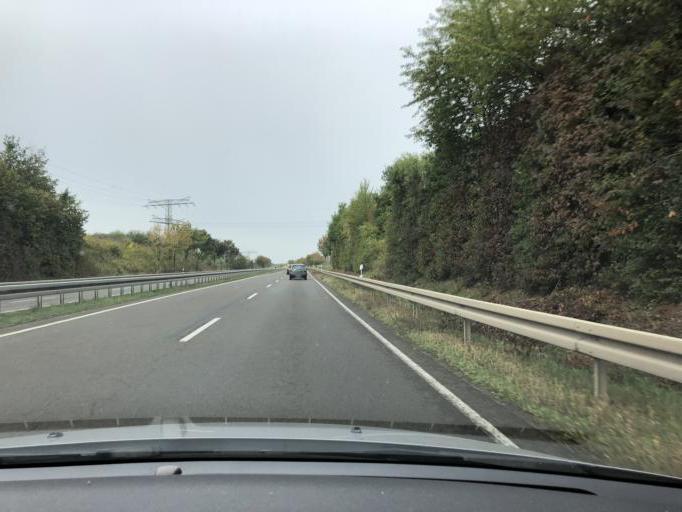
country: DE
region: Saxony
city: Schkeuditz
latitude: 51.3942
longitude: 12.2853
